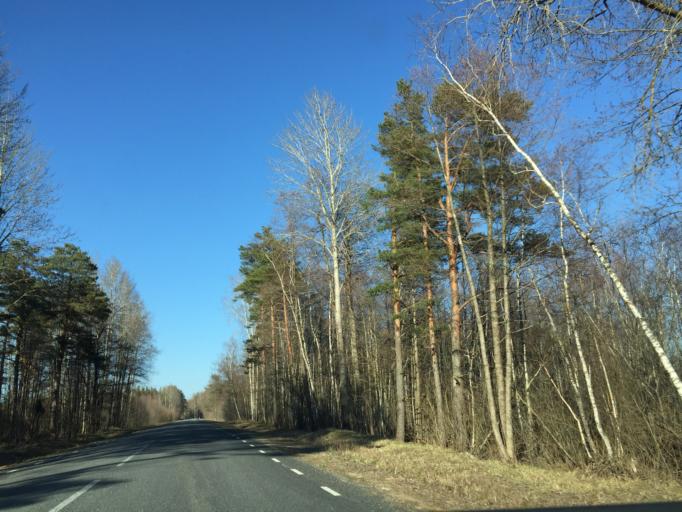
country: RU
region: Pskov
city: Gdov
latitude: 59.0143
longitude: 27.6832
